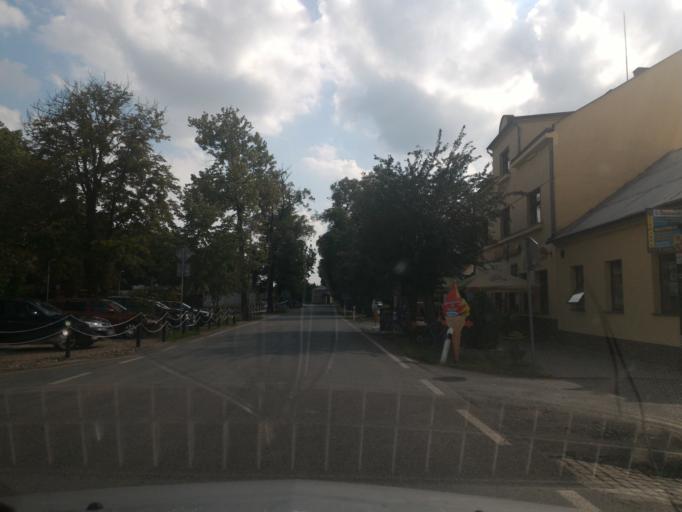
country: CZ
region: Central Bohemia
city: Loucen
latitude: 50.2873
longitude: 15.0217
